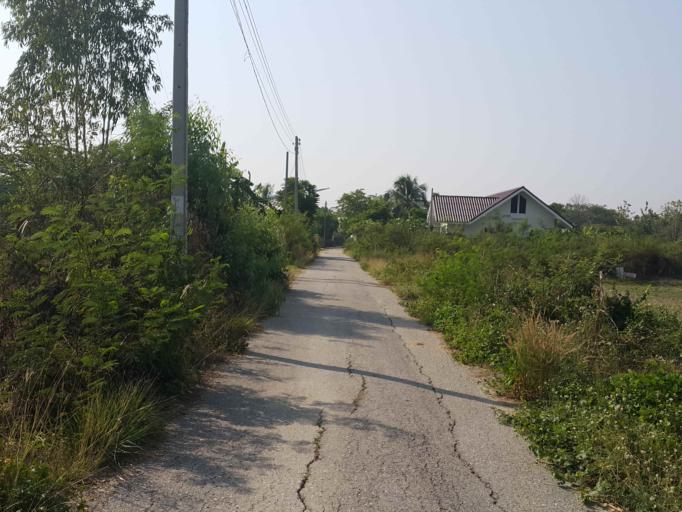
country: TH
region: Chiang Mai
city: San Kamphaeng
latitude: 18.7629
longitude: 99.0766
